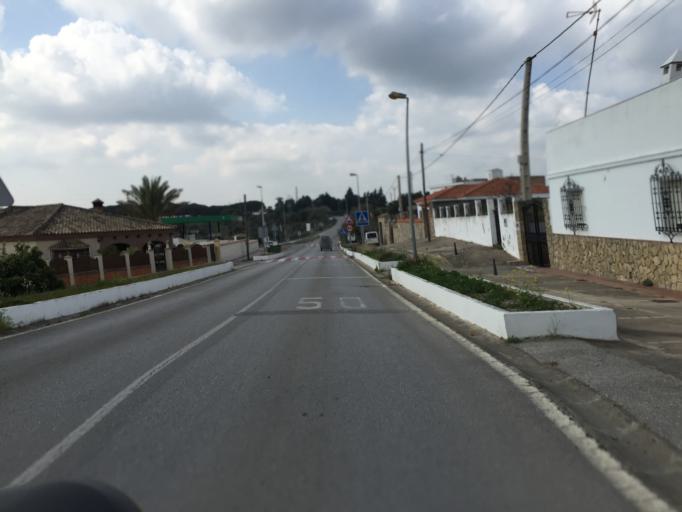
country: ES
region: Andalusia
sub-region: Provincia de Cadiz
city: Benalup-Casas Viejas
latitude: 36.3146
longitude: -5.8856
